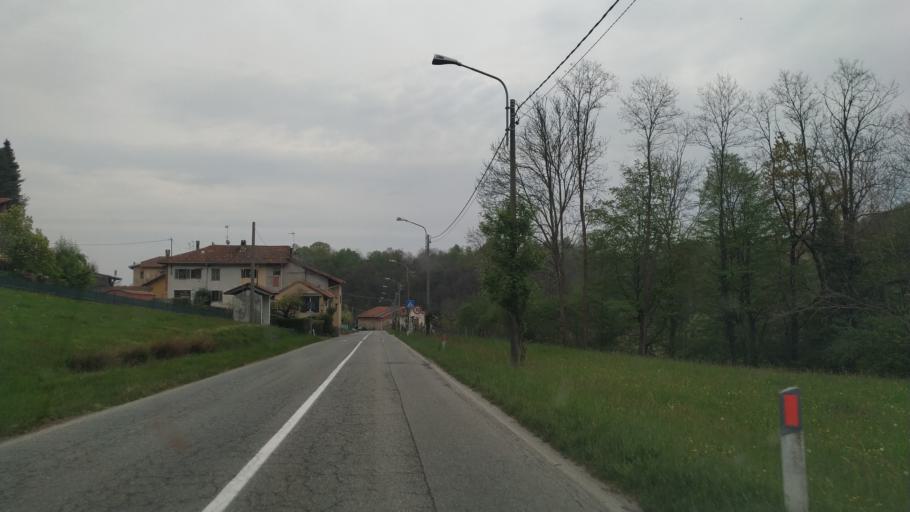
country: IT
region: Piedmont
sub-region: Provincia di Biella
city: Occhieppo Superiore
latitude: 45.5705
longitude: 8.0151
